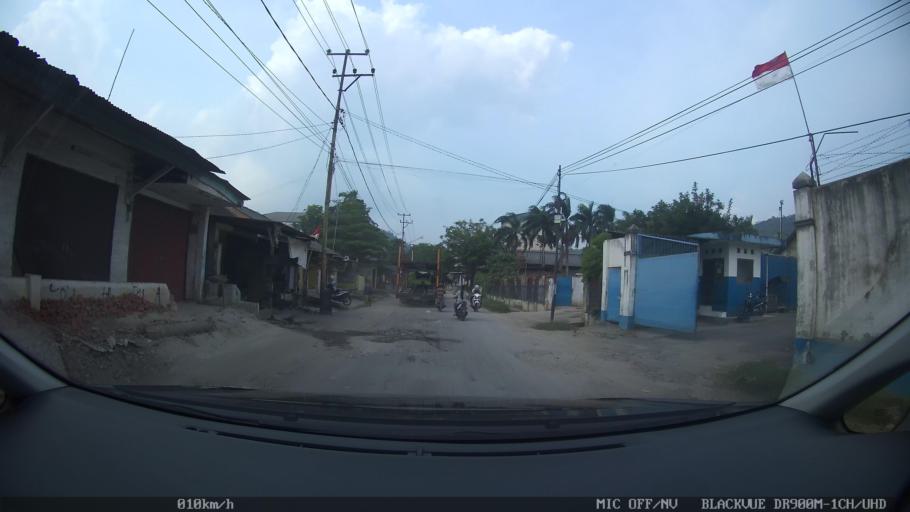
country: ID
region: Lampung
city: Panjang
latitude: -5.4514
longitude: 105.3080
